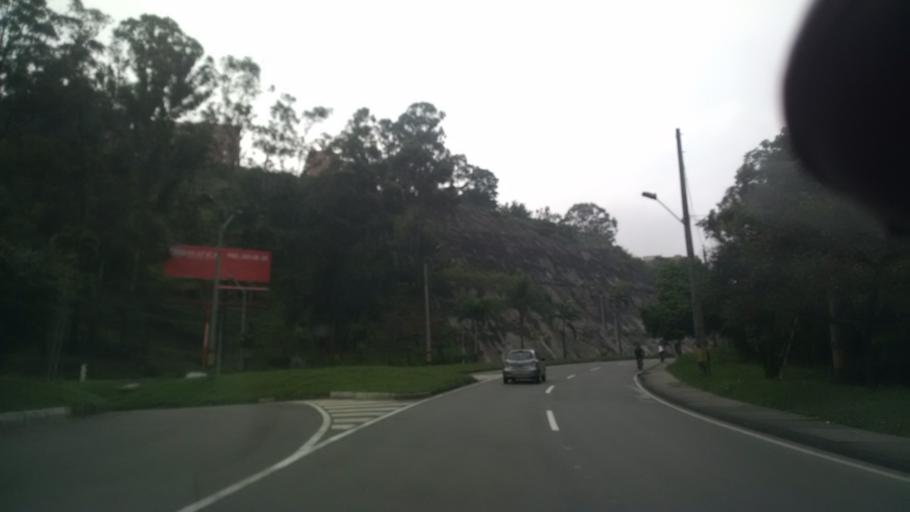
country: CO
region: Antioquia
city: Medellin
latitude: 6.2314
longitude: -75.5660
